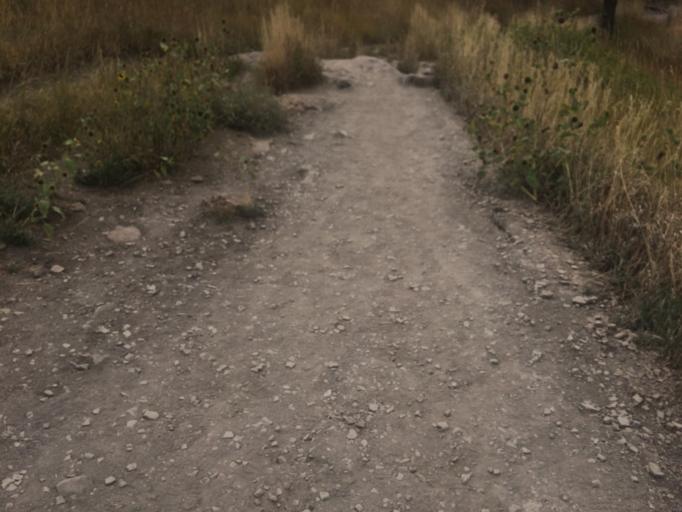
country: US
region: Colorado
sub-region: Boulder County
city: Boulder
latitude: 39.9778
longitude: -105.2799
